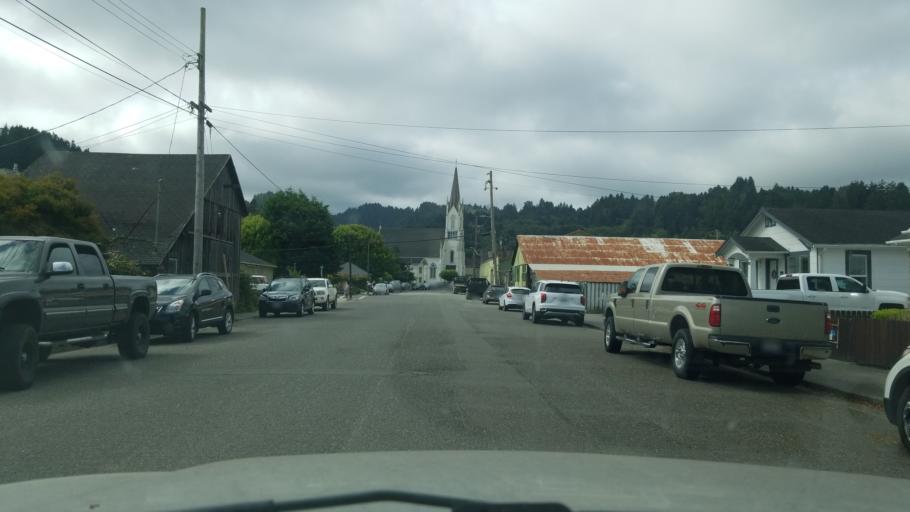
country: US
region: California
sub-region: Humboldt County
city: Ferndale
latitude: 40.5782
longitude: -124.2605
